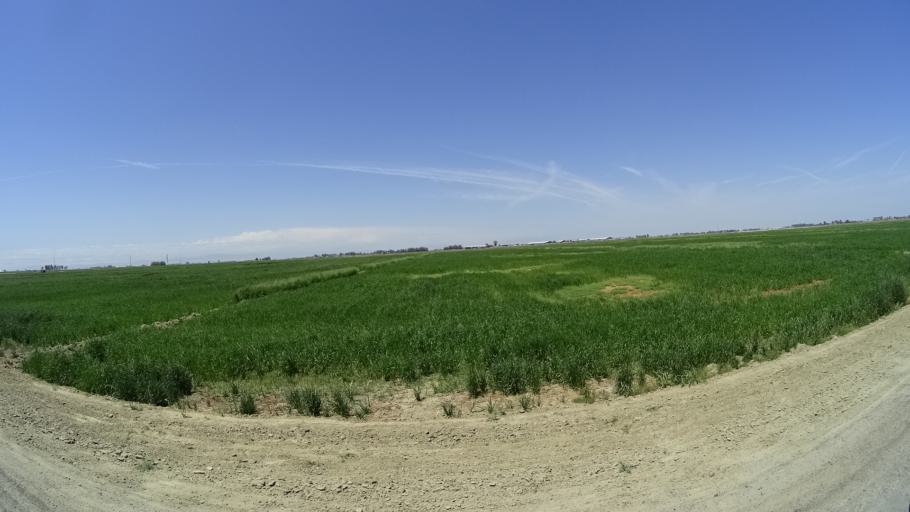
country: US
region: California
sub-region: Kings County
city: Stratford
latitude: 36.2062
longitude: -119.7445
